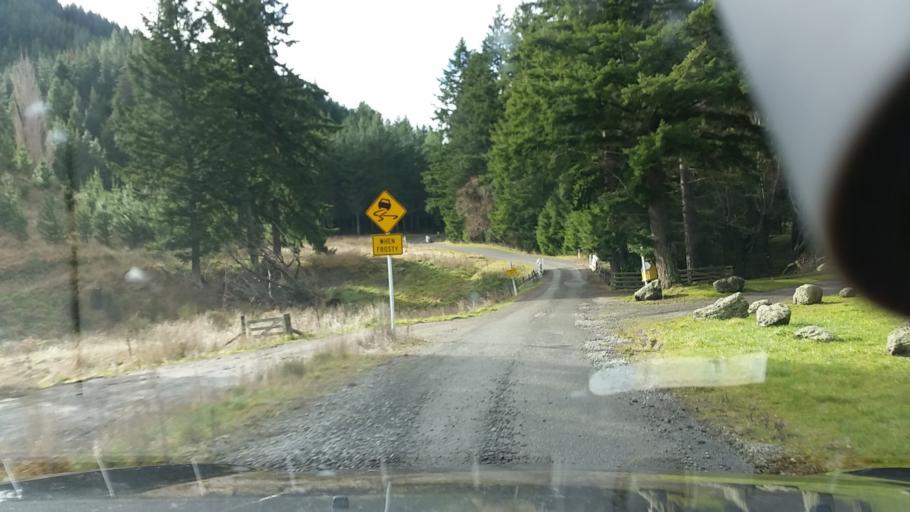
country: NZ
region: Nelson
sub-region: Nelson City
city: Nelson
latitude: -41.7052
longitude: 173.4841
